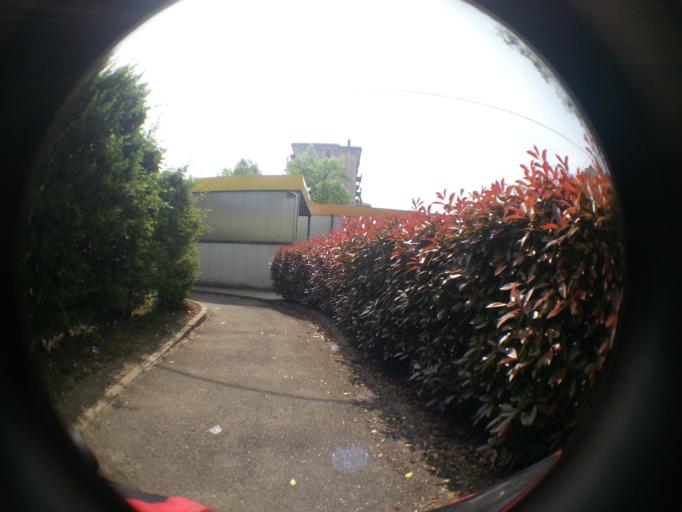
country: IT
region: Lombardy
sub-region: Citta metropolitana di Milano
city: Cusano Milanino
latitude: 45.5547
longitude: 9.1857
